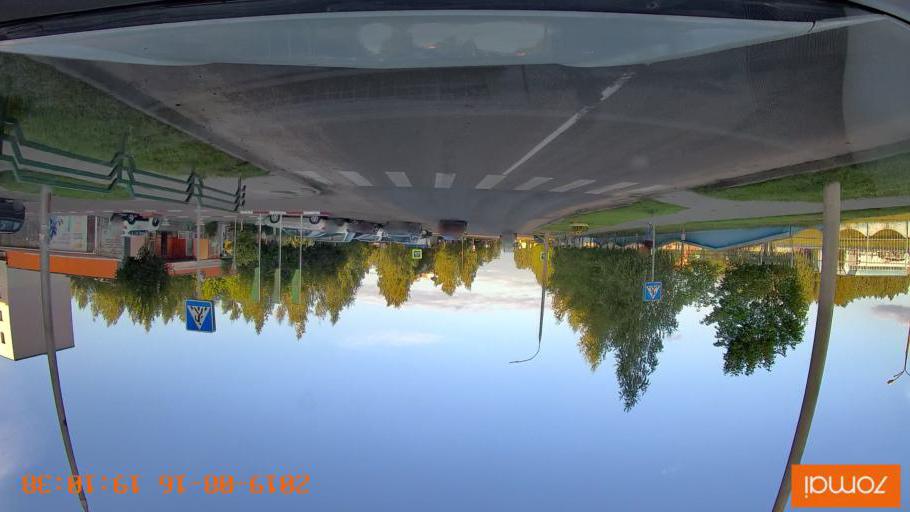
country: BY
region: Mogilev
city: Asipovichy
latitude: 53.3233
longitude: 28.6428
